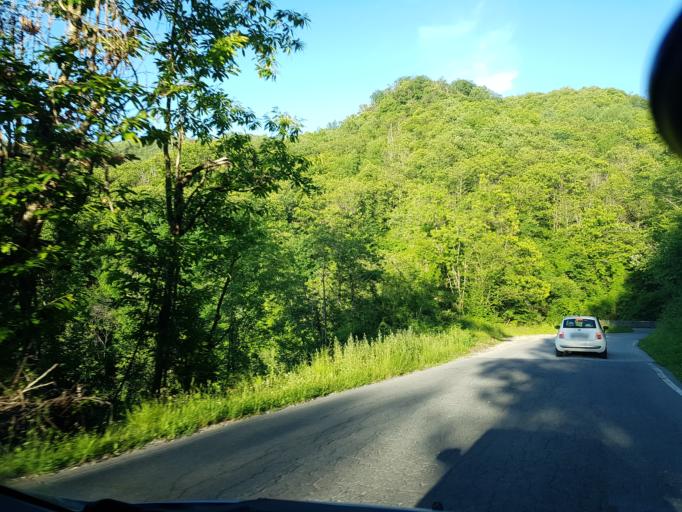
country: IT
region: Tuscany
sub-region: Provincia di Lucca
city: Minucciano
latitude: 44.1785
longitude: 10.2011
